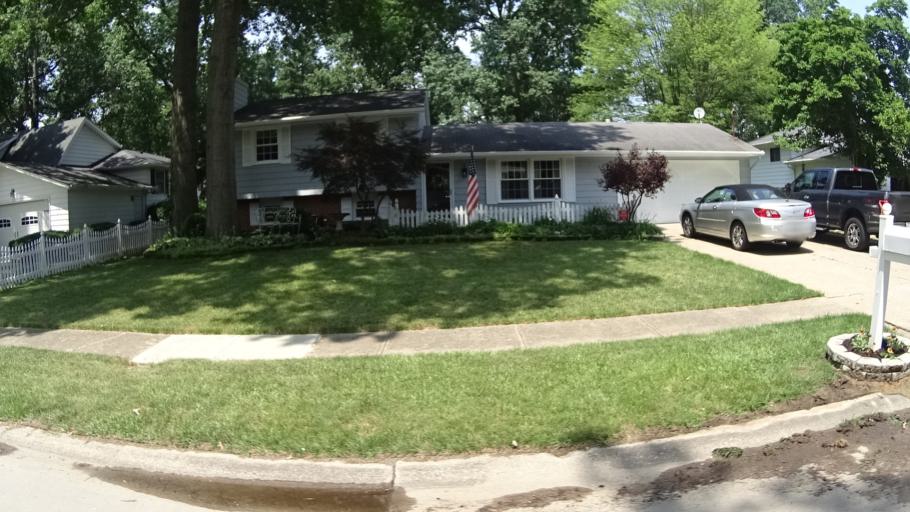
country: US
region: Ohio
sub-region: Lorain County
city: Vermilion
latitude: 41.4052
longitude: -82.3546
